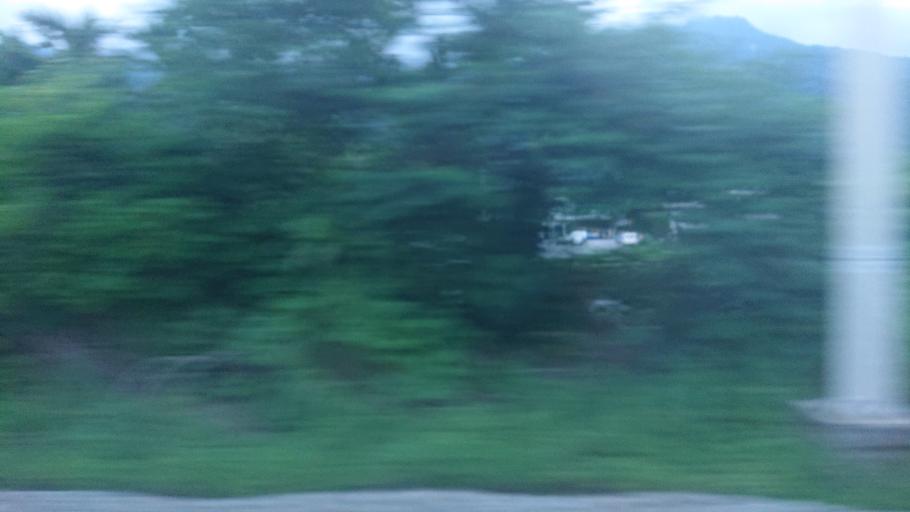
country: TW
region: Taiwan
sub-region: Taitung
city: Taitung
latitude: 23.0435
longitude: 121.1638
